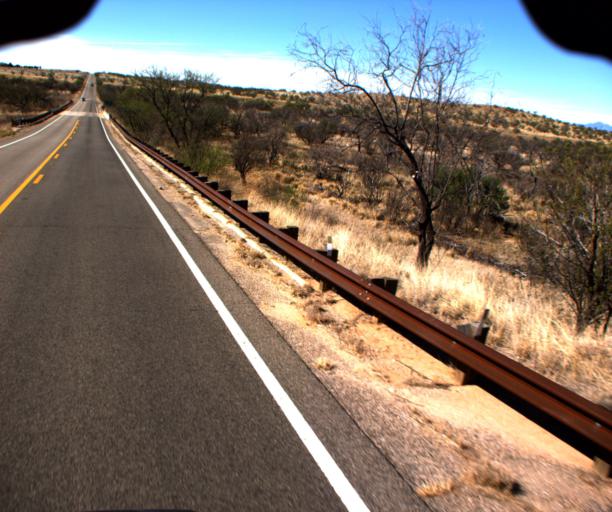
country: US
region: Arizona
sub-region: Pima County
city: Corona de Tucson
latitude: 31.7349
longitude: -110.6617
